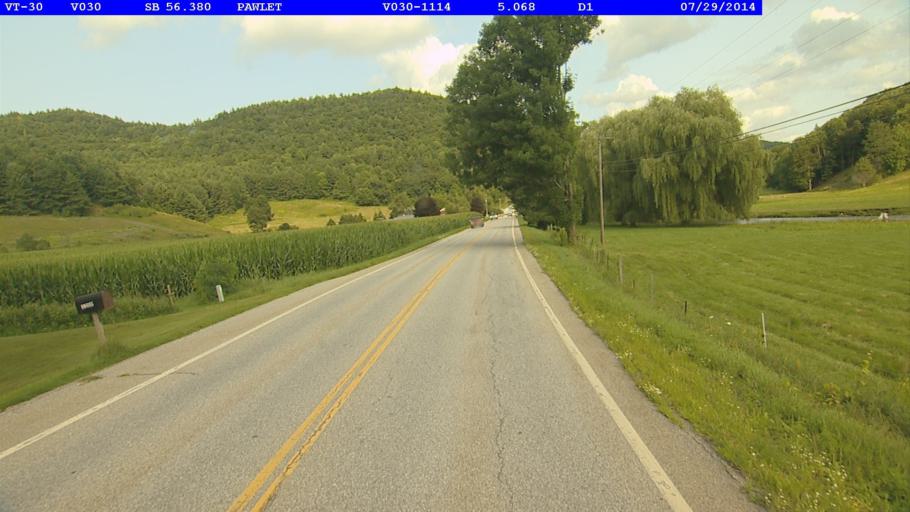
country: US
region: New York
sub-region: Washington County
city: Granville
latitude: 43.3755
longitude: -73.1970
